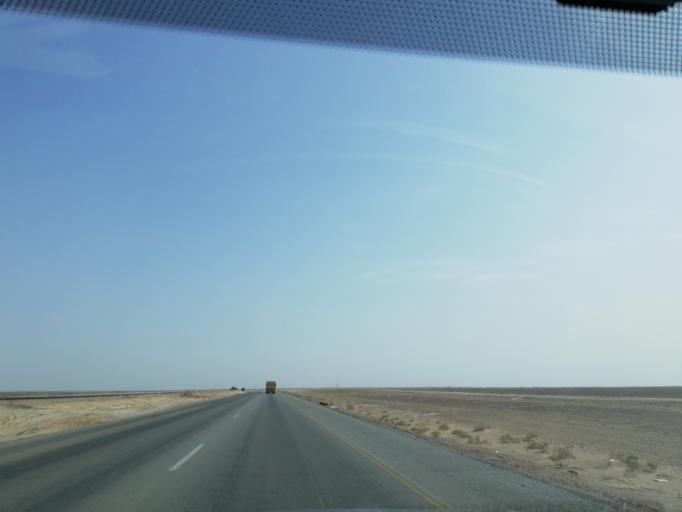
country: OM
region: Muhafazat ad Dakhiliyah
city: Adam
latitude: 21.5998
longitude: 57.2954
